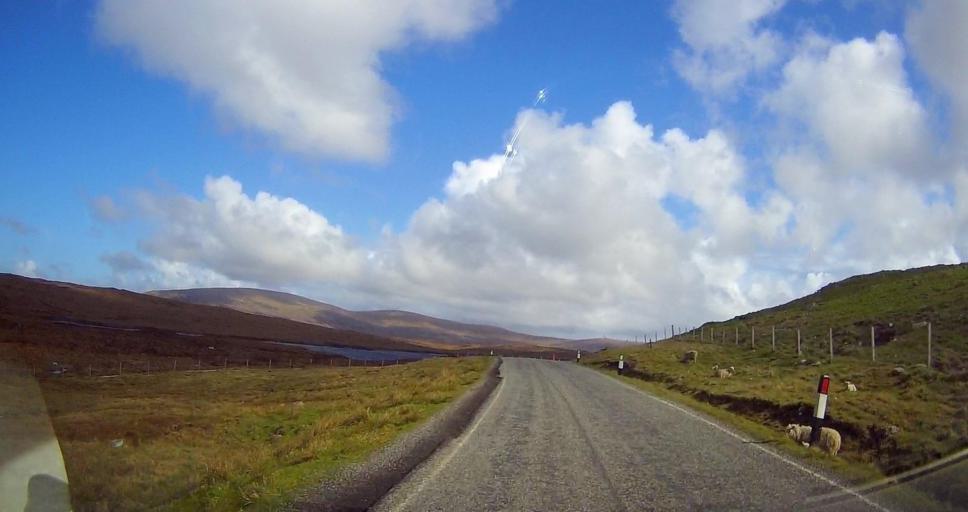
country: GB
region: Scotland
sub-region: Shetland Islands
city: Lerwick
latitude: 60.4843
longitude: -1.4030
